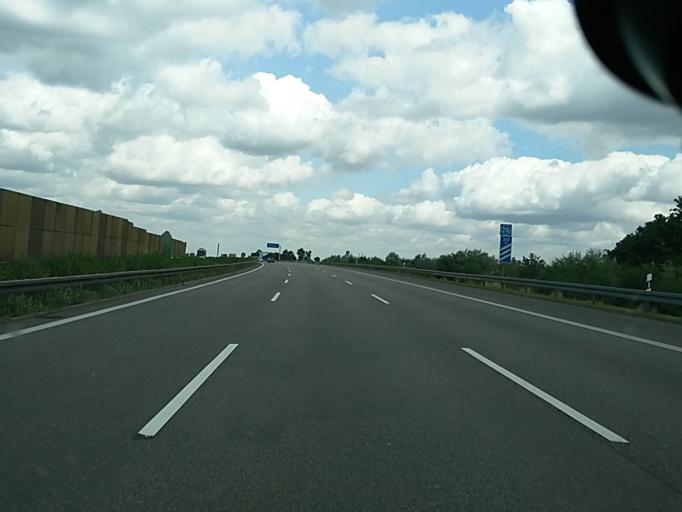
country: DE
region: Thuringia
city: Walpernhain
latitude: 51.0346
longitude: 11.9399
